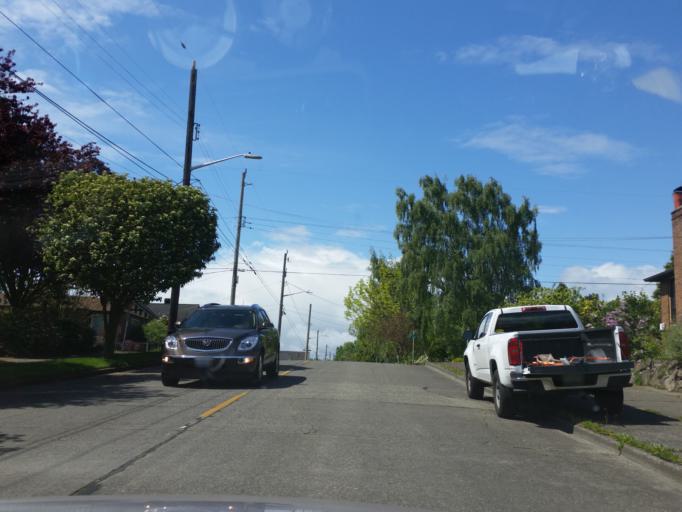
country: US
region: Washington
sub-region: King County
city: Shoreline
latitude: 47.6868
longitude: -122.3965
